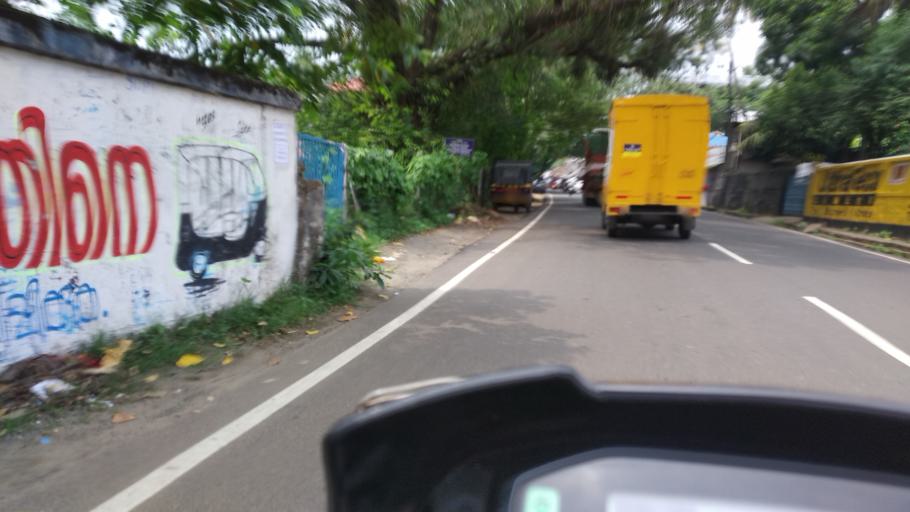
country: IN
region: Kerala
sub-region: Ernakulam
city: Perumpavur
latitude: 10.1176
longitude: 76.4784
